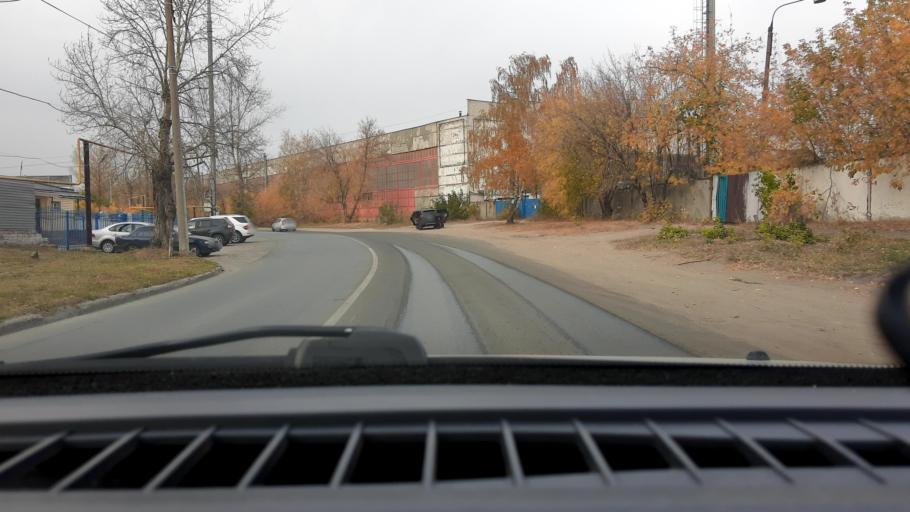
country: RU
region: Nizjnij Novgorod
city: Gorbatovka
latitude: 56.3460
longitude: 43.8233
